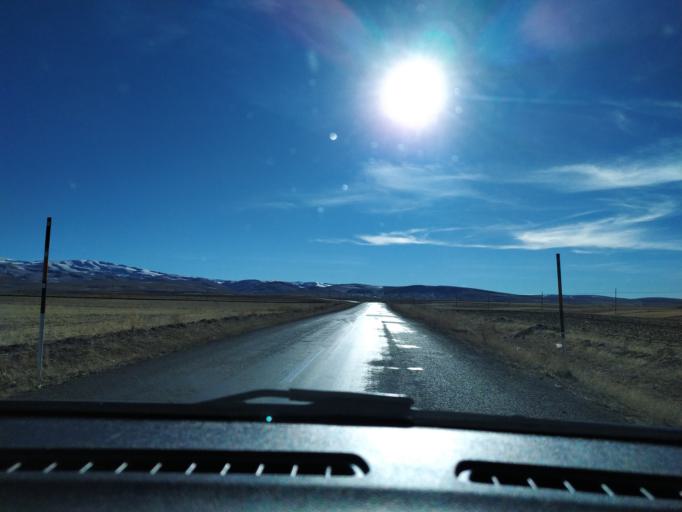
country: TR
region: Kayseri
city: Orensehir
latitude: 38.8828
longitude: 36.7275
